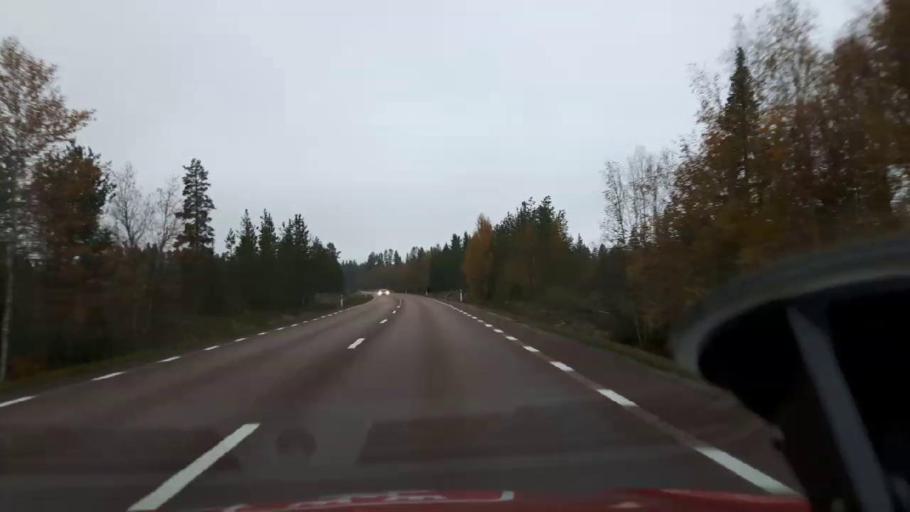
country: SE
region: Jaemtland
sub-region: Bergs Kommun
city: Hoverberg
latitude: 62.5096
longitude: 14.4497
